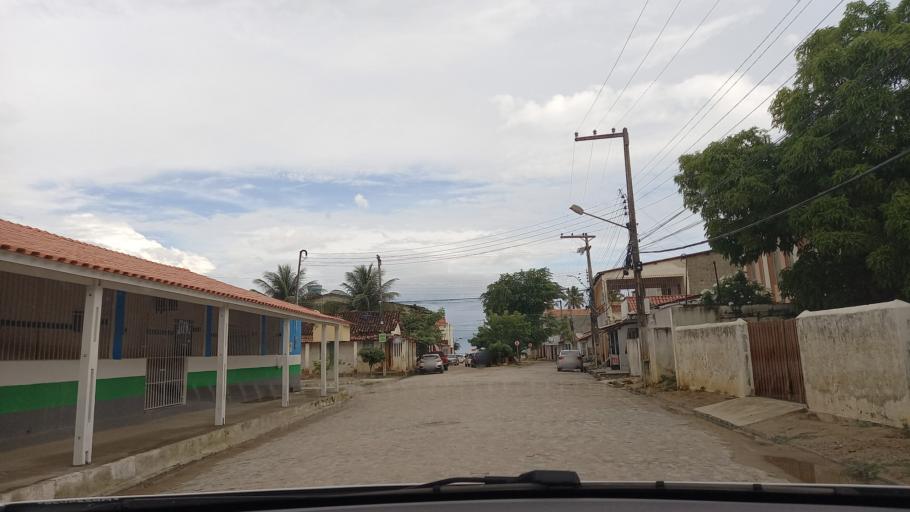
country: BR
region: Alagoas
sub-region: Maragogi
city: Maragogi
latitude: -8.9863
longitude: -35.1945
